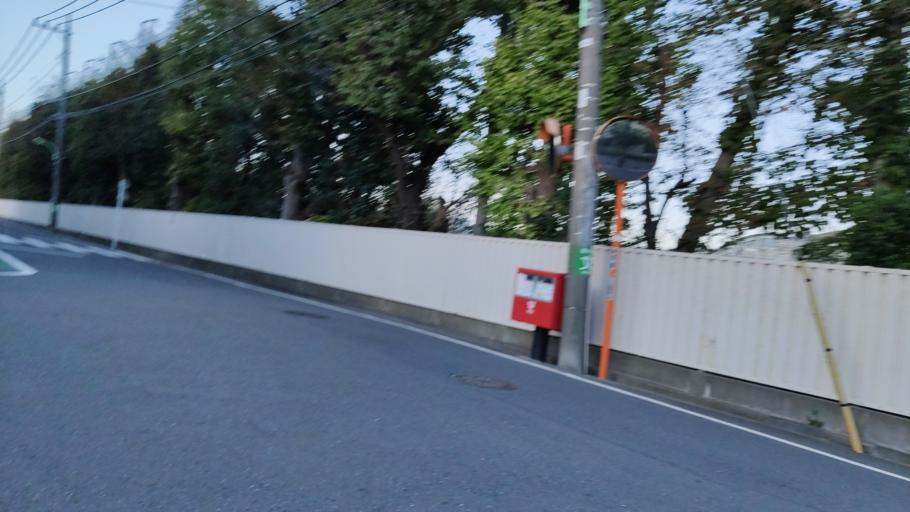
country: JP
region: Tokyo
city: Tokyo
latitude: 35.6534
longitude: 139.6802
